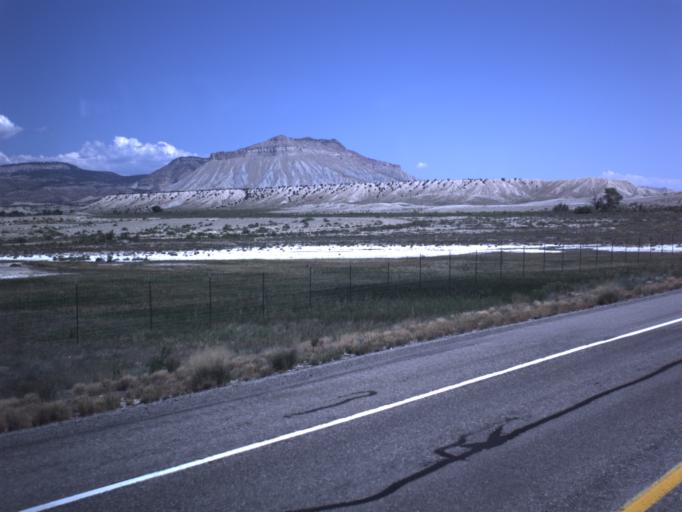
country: US
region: Utah
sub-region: Emery County
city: Ferron
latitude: 38.9430
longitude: -111.2189
